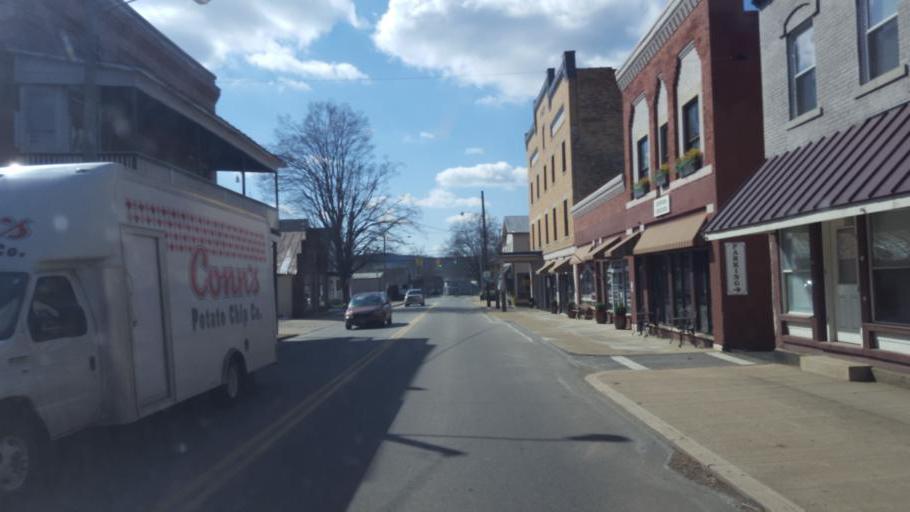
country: US
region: Ohio
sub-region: Licking County
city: Utica
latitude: 40.2334
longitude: -82.4528
